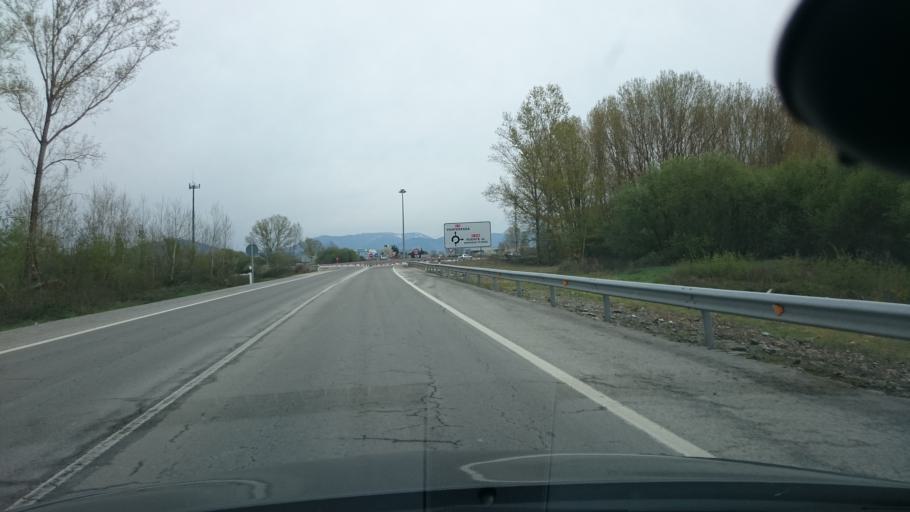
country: ES
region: Castille and Leon
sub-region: Provincia de Leon
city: Camponaraya
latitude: 42.5660
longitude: -6.6525
